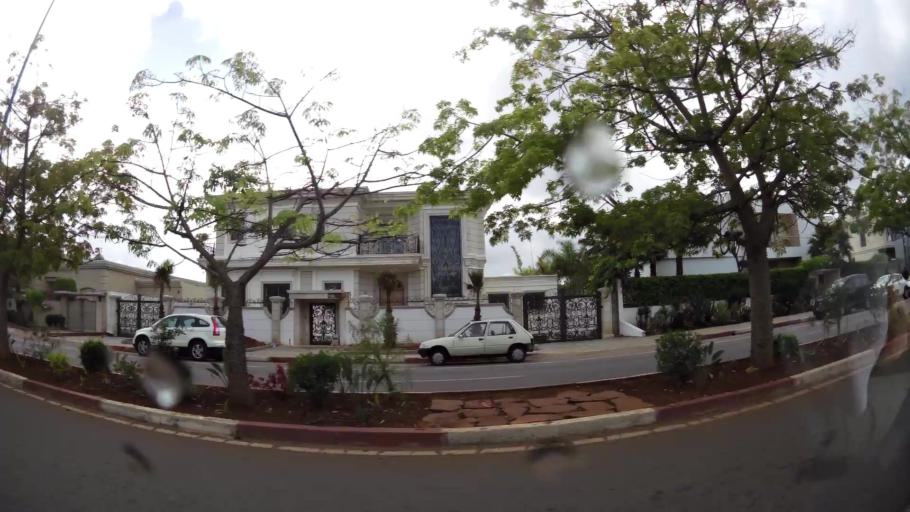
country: MA
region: Grand Casablanca
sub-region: Casablanca
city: Casablanca
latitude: 33.5452
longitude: -7.6315
